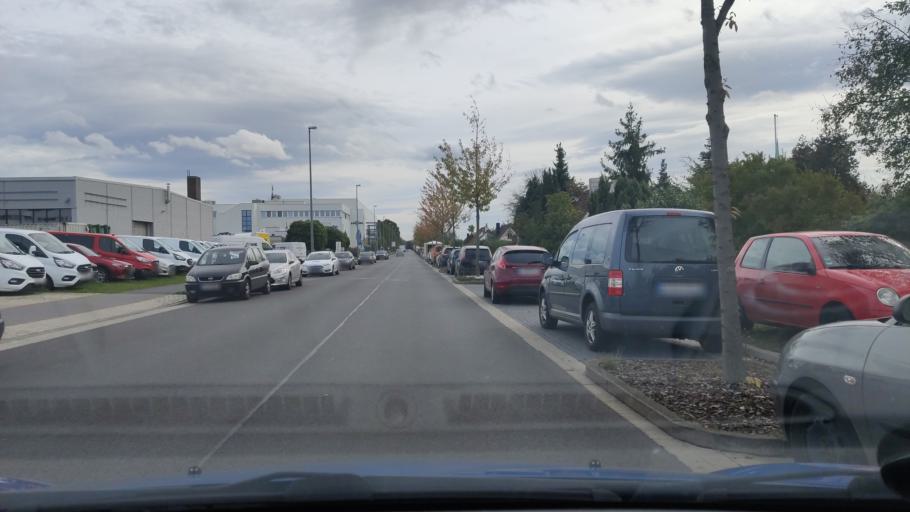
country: DE
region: Lower Saxony
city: Hannover
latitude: 52.4080
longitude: 9.7021
